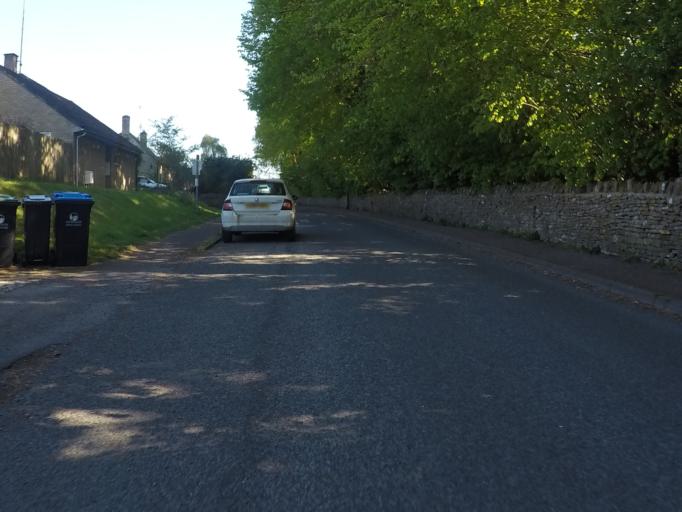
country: GB
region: England
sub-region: Oxfordshire
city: Charlbury
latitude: 51.8687
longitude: -1.4791
